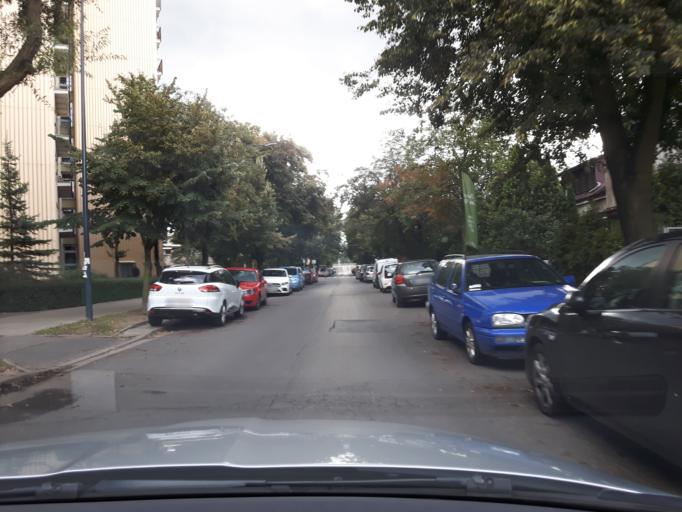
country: PL
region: Masovian Voivodeship
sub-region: Warszawa
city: Praga Poludnie
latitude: 52.2241
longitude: 21.0665
